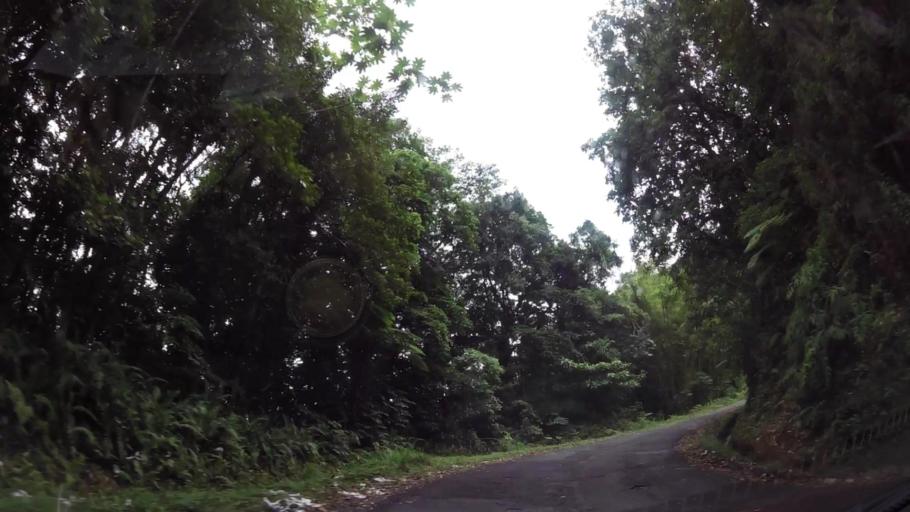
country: DM
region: Saint Paul
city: Pont Casse
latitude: 15.3975
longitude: -61.3102
